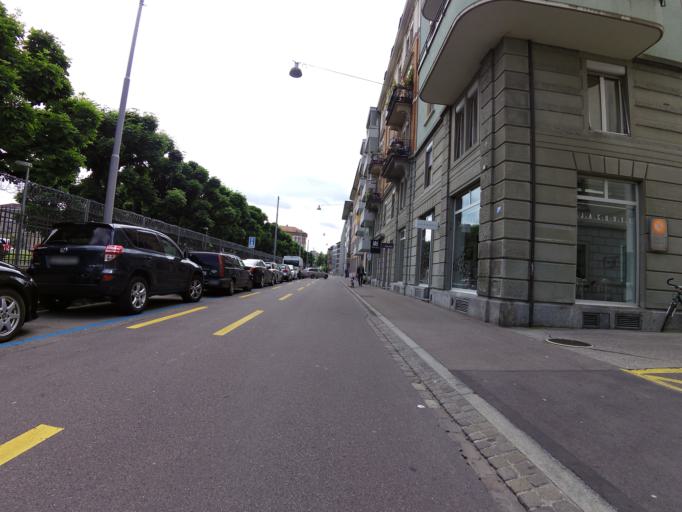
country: CH
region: Zurich
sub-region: Bezirk Zuerich
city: Zuerich (Kreis 4) / Langstrasse
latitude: 47.3762
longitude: 8.5298
